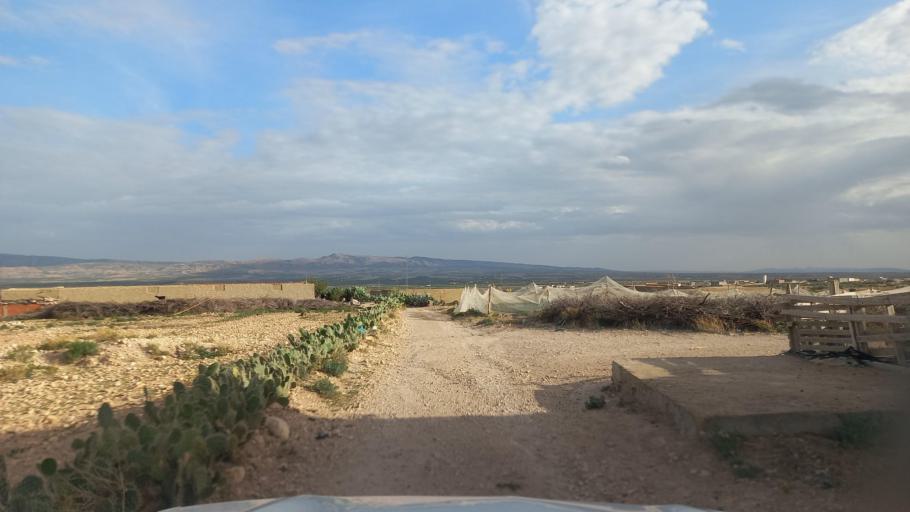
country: TN
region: Al Qasrayn
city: Sbiba
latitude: 35.4563
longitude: 9.0781
